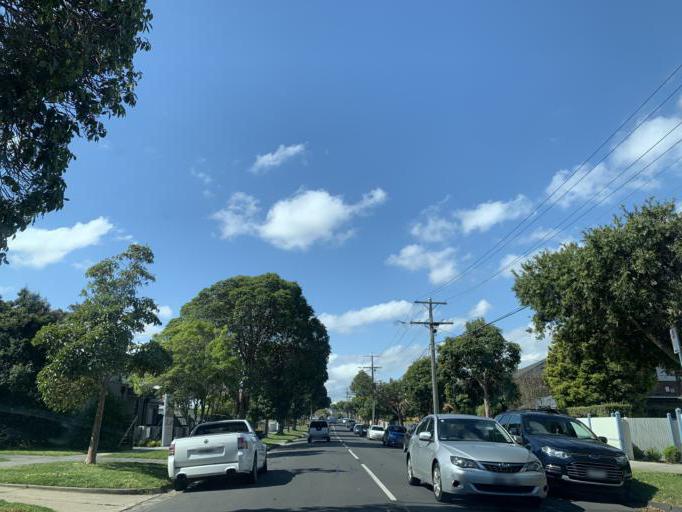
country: AU
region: Victoria
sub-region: Kingston
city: Parkdale
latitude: -37.9921
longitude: 145.0792
